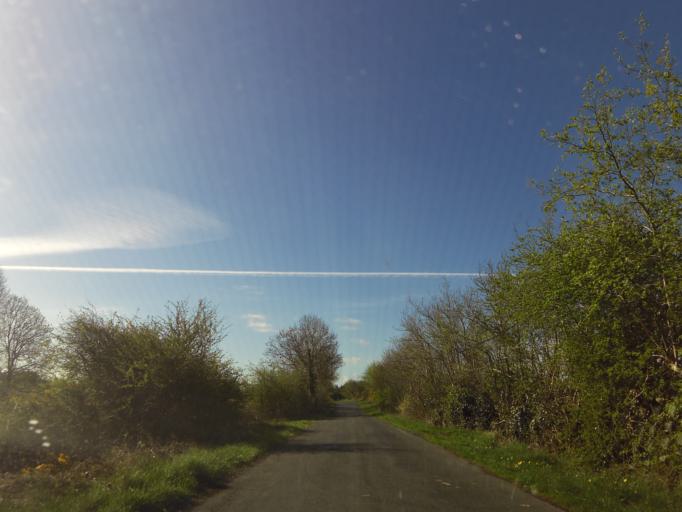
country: IE
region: Connaught
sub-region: Maigh Eo
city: Claremorris
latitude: 53.7794
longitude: -8.9609
